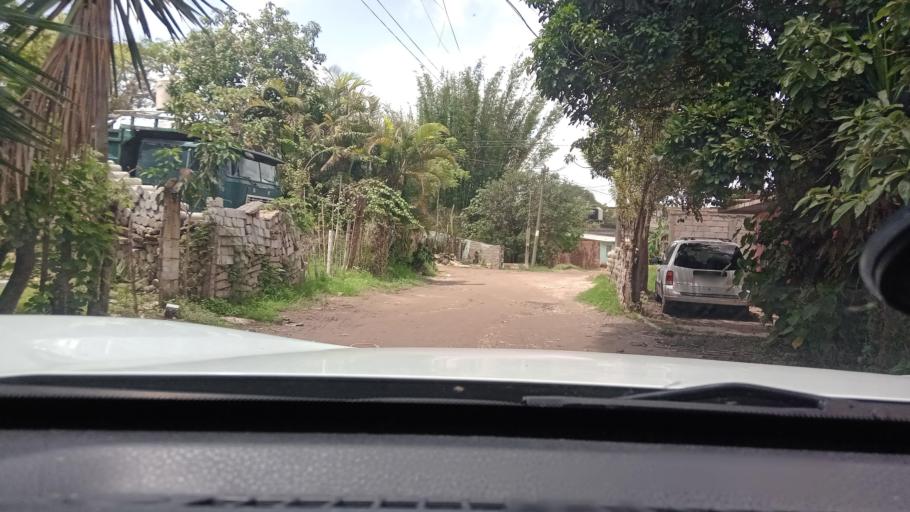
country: MX
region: Veracruz
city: El Castillo
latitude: 19.5492
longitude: -96.8605
